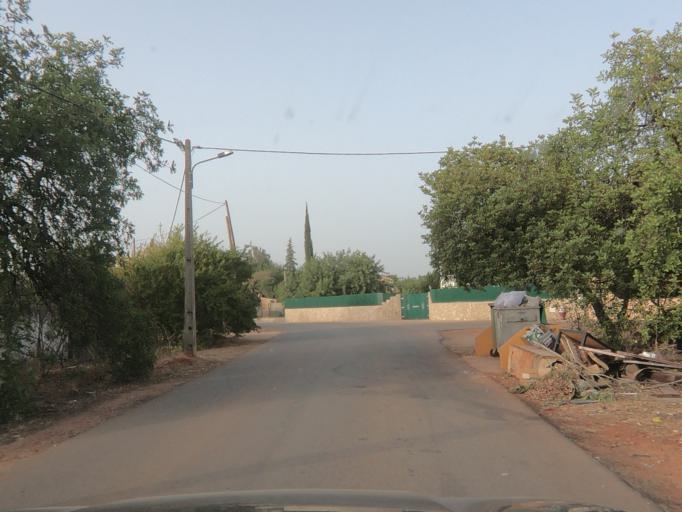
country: PT
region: Faro
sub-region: Loule
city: Vilamoura
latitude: 37.1129
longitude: -8.0866
